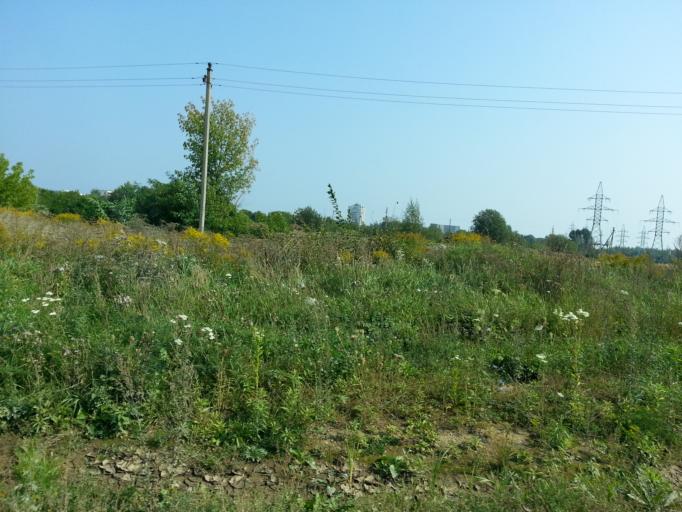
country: LT
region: Vilnius County
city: Justiniskes
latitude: 54.7264
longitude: 25.2061
